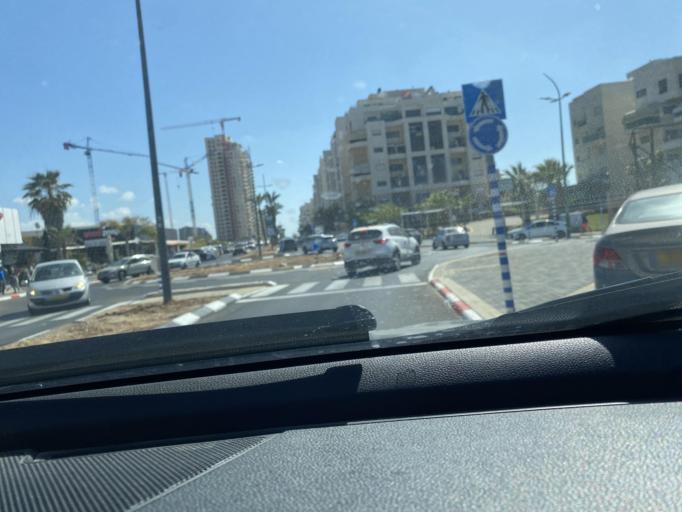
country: IL
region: Southern District
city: Ashqelon
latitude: 31.6832
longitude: 34.5604
